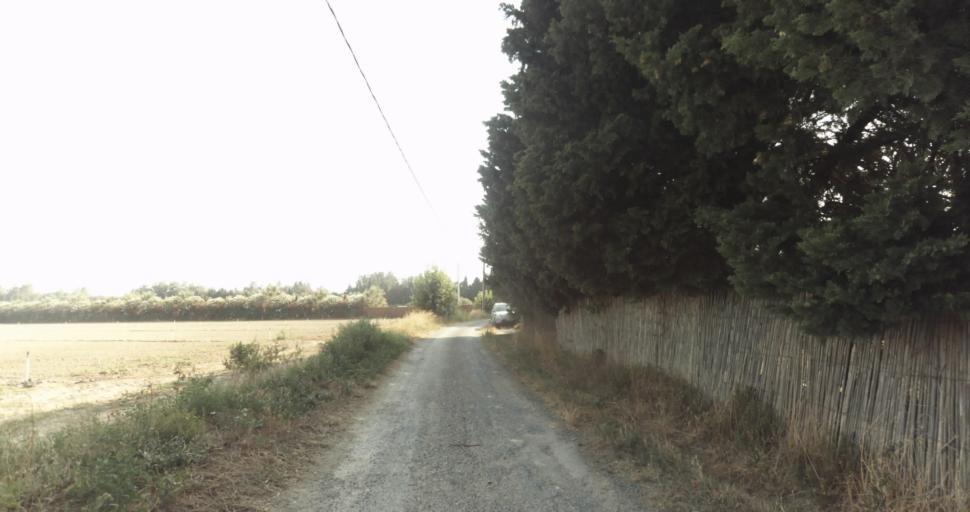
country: FR
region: Languedoc-Roussillon
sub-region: Departement des Pyrenees-Orientales
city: Latour-Bas-Elne
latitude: 42.6006
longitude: 3.0196
